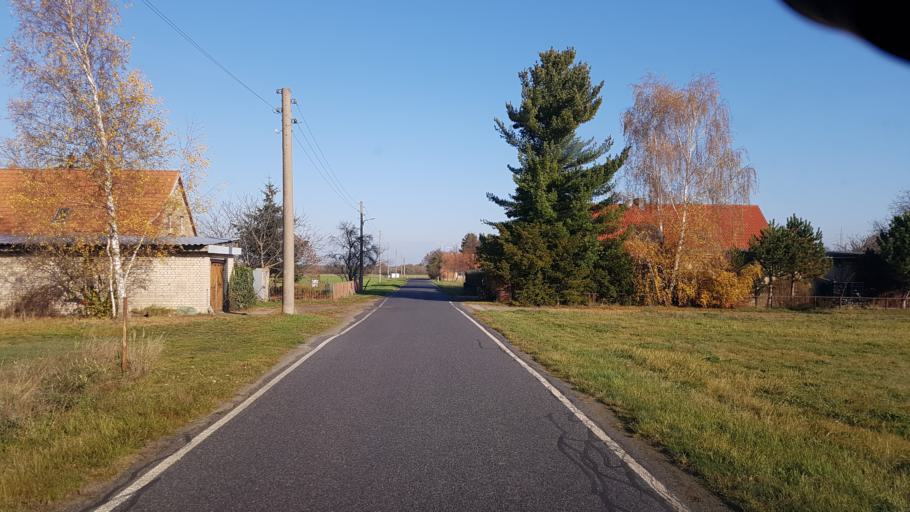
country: DE
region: Brandenburg
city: Grossraschen
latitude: 51.5793
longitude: 13.9410
